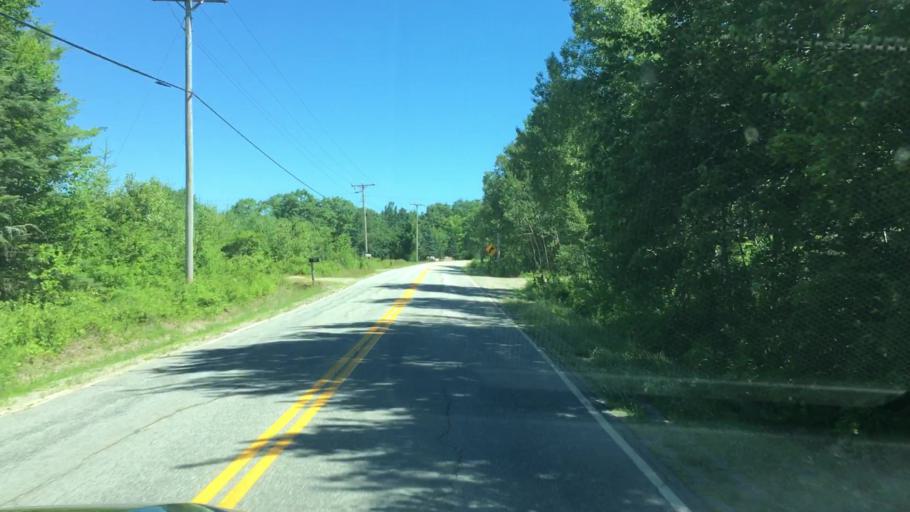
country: US
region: Maine
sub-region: Hancock County
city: Penobscot
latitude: 44.5157
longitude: -68.6706
